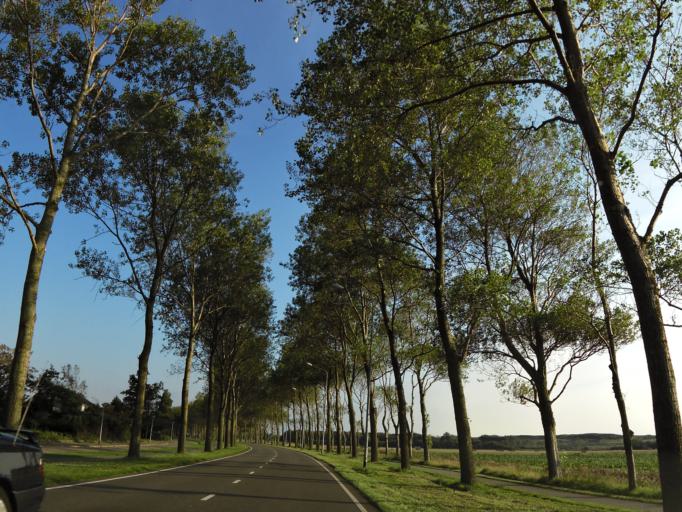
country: NL
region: Zeeland
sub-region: Gemeente Vlissingen
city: Vlissingen
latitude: 51.4641
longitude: 3.5401
